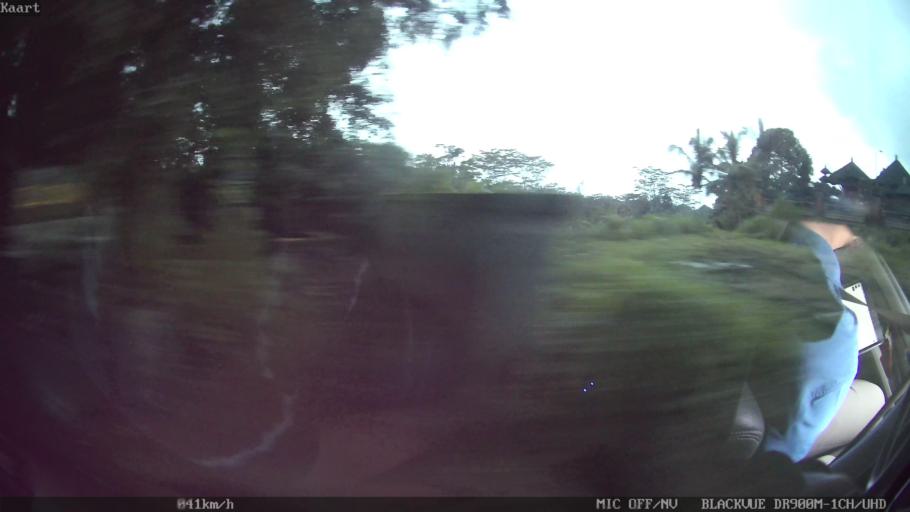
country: ID
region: Bali
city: Bayad
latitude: -8.4457
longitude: 115.2422
